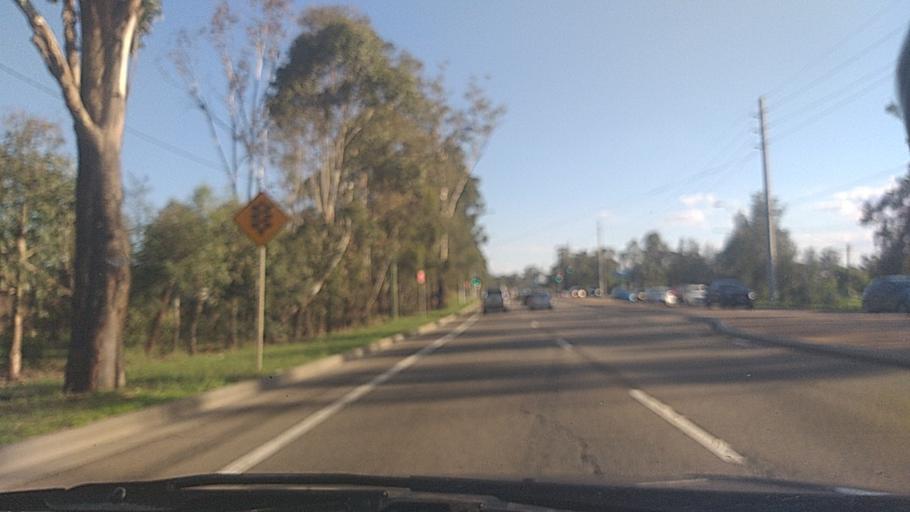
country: AU
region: New South Wales
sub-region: Penrith Municipality
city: Werrington Downs
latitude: -33.7338
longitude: 150.7179
